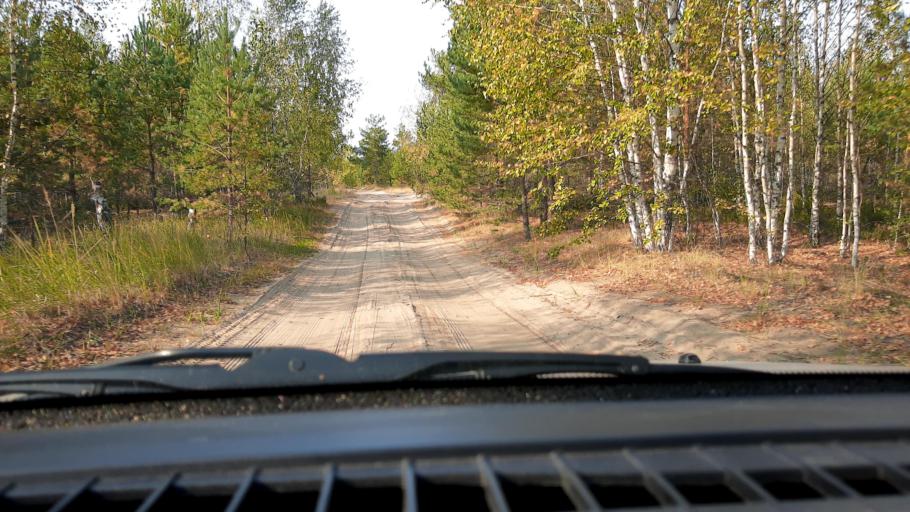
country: RU
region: Nizjnij Novgorod
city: Lukino
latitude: 56.3908
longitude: 43.6029
